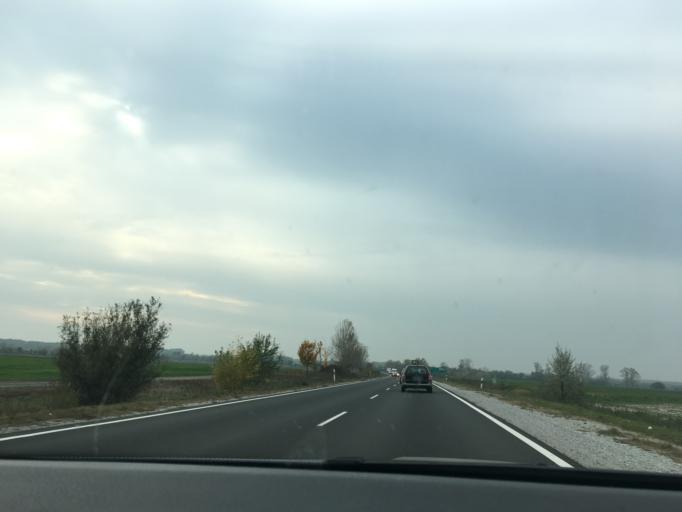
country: HU
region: Pest
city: Abony
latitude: 47.2193
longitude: 19.9883
